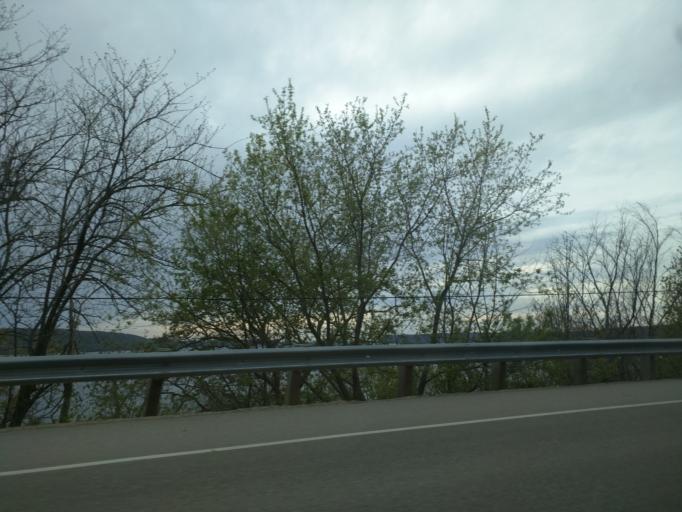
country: US
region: Minnesota
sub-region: Wabasha County
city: Lake City
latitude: 44.5478
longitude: -92.2991
